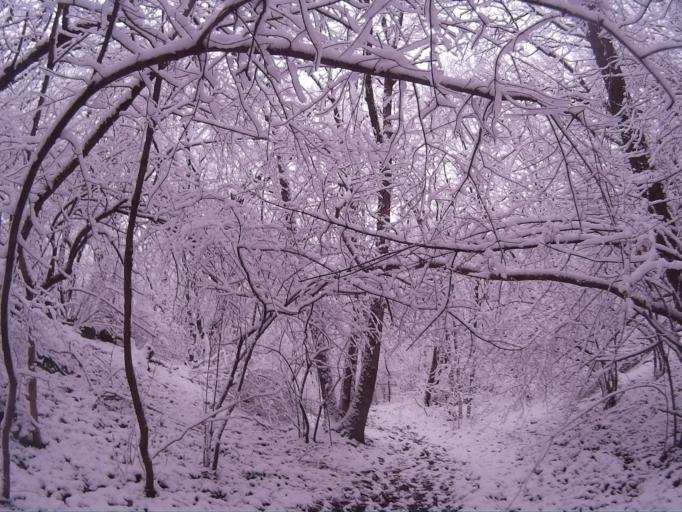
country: HU
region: Fejer
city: Szarliget
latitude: 47.5204
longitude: 18.5013
